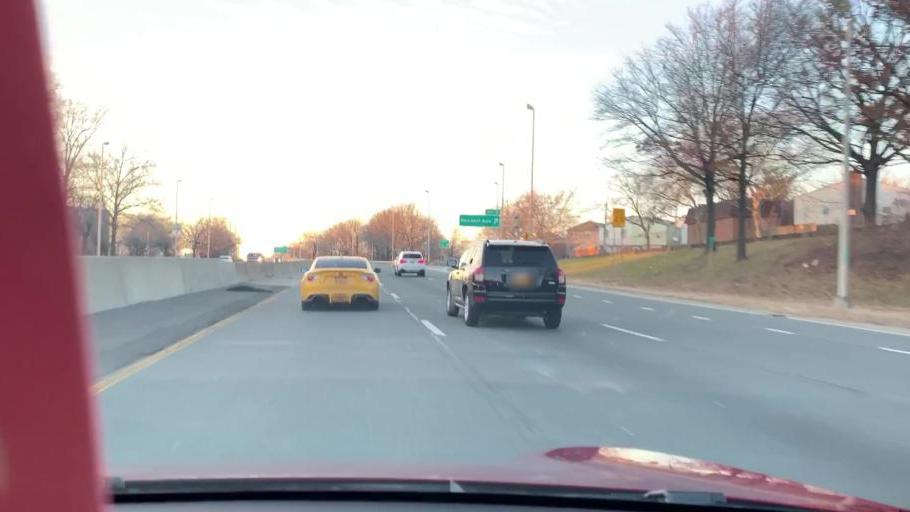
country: US
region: New York
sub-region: Bronx
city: The Bronx
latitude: 40.8233
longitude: -73.8208
